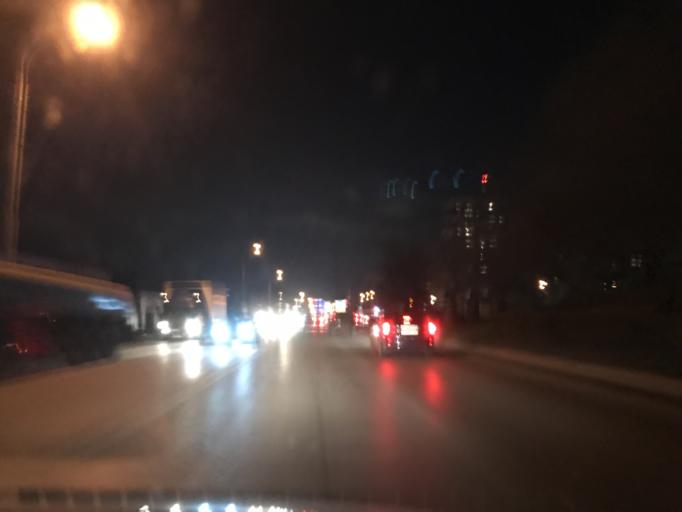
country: RU
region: Rostov
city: Kalinin
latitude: 47.2099
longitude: 39.6136
